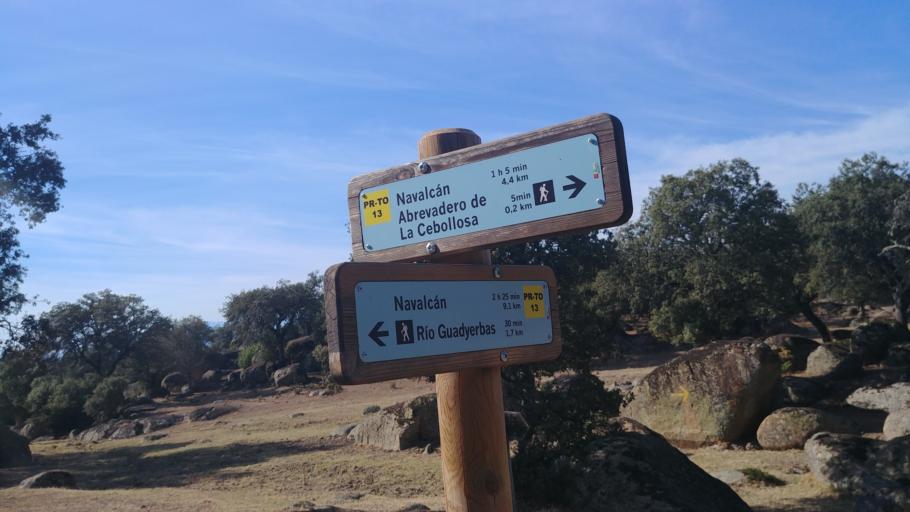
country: ES
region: Castille-La Mancha
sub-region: Province of Toledo
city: Navalcan
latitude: 40.0631
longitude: -5.1408
